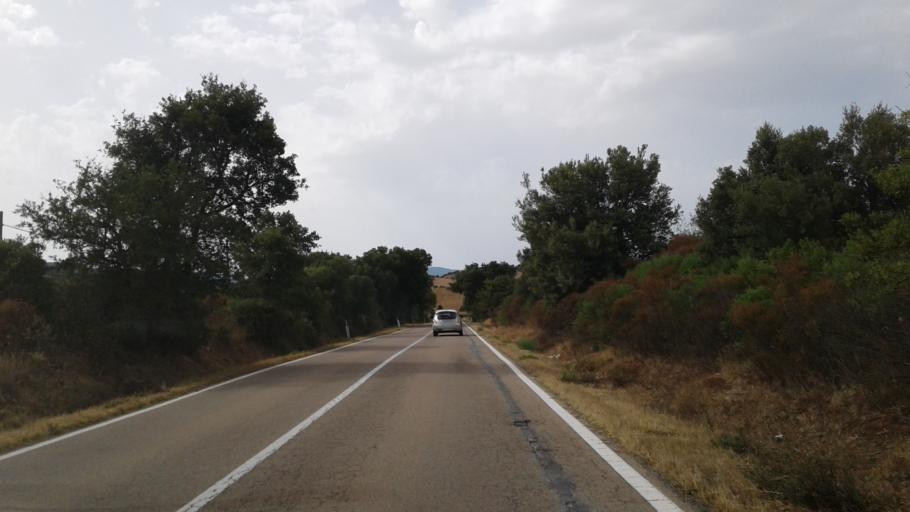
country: IT
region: Sardinia
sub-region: Provincia di Olbia-Tempio
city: Sant'Antonio di Gallura
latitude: 40.9444
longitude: 9.3002
